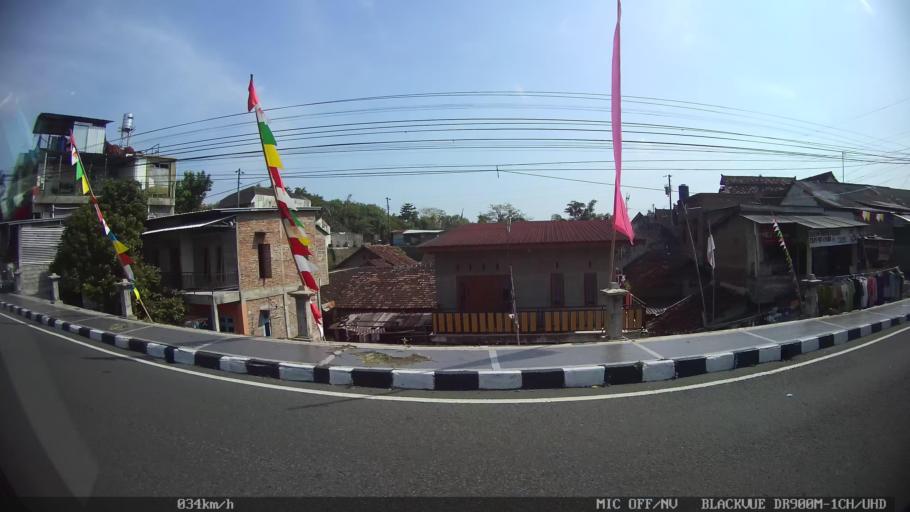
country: ID
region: Daerah Istimewa Yogyakarta
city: Yogyakarta
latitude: -7.7903
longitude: 110.3555
